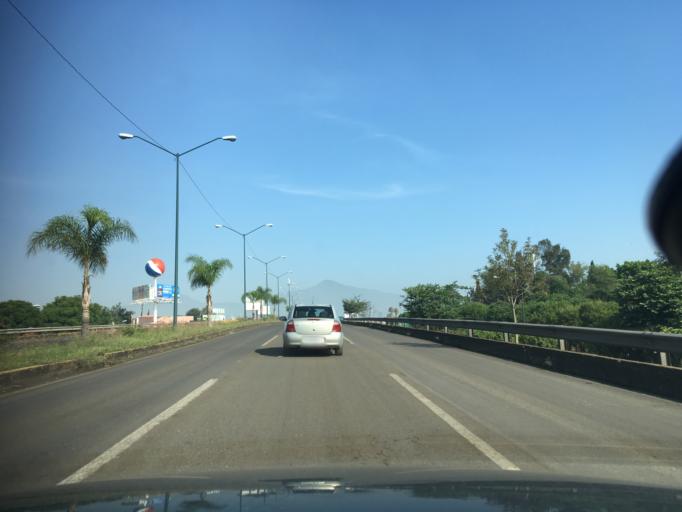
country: MX
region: Michoacan
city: Morelia
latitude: 19.7207
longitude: -101.1868
